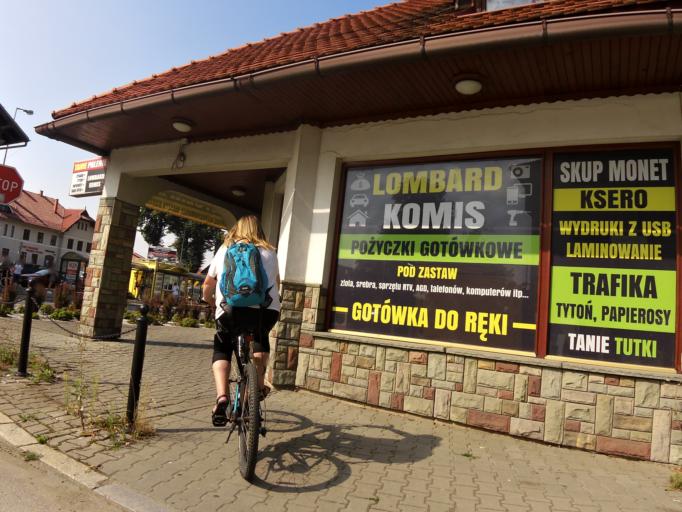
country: PL
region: Silesian Voivodeship
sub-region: Powiat zywiecki
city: Zywiec
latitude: 49.6790
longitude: 19.1871
